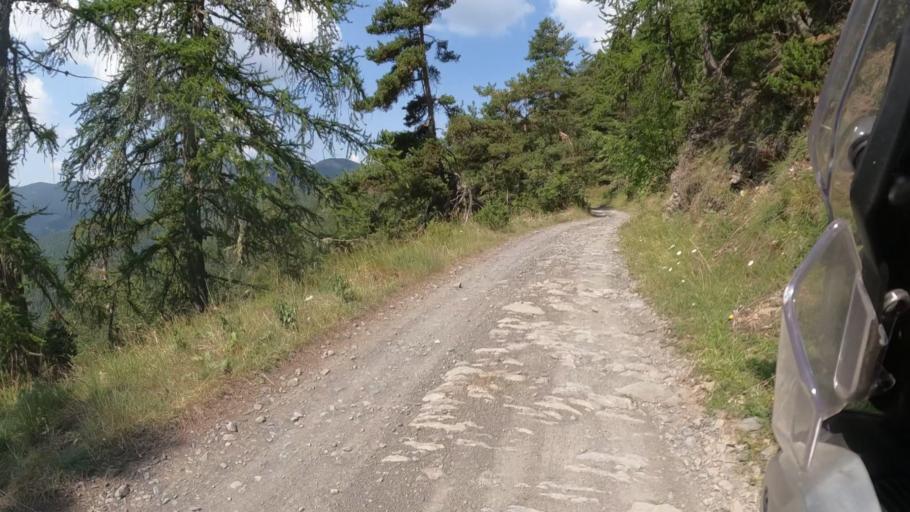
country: IT
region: Piedmont
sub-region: Provincia di Cuneo
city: Briga Alta
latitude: 44.0388
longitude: 7.6926
